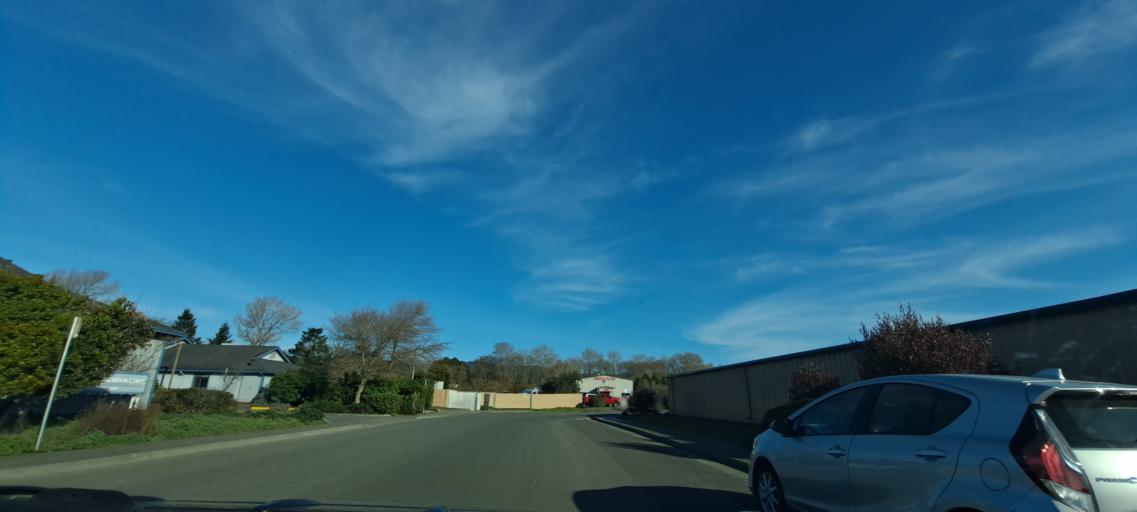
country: US
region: California
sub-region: Humboldt County
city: Fortuna
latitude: 40.5806
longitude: -124.1530
